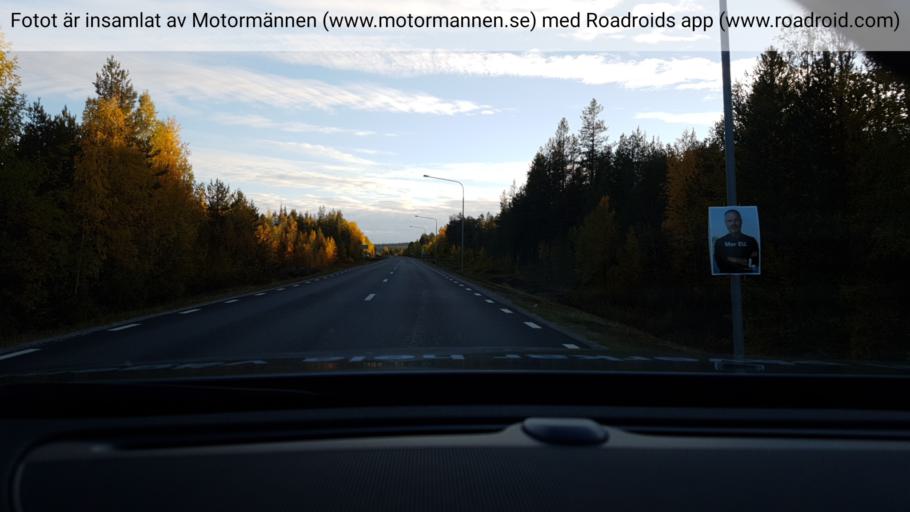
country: SE
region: Norrbotten
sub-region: Jokkmokks Kommun
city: Jokkmokk
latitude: 66.6006
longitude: 19.8149
